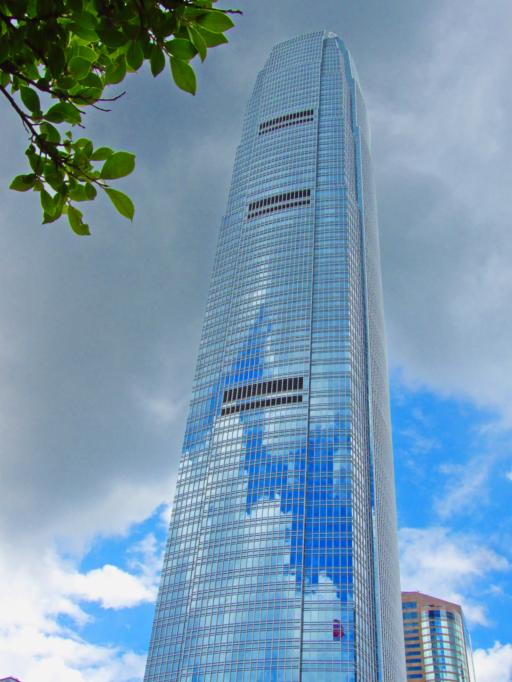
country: HK
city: Hong Kong
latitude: 22.2875
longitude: 114.1587
